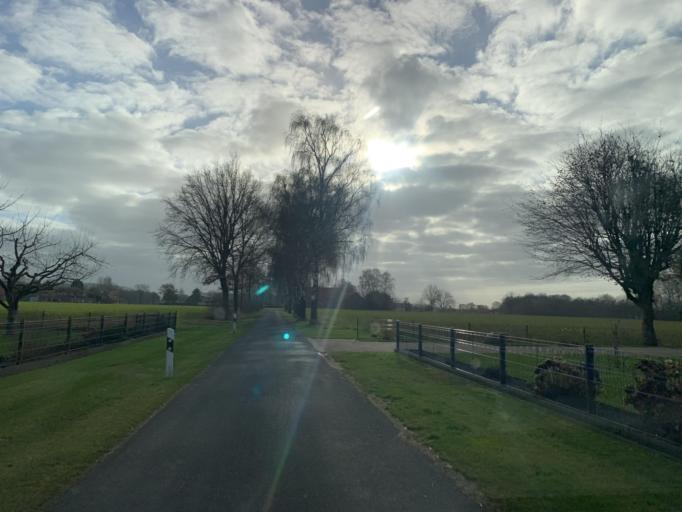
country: DE
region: North Rhine-Westphalia
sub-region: Regierungsbezirk Munster
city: Greven
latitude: 52.0534
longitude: 7.6337
